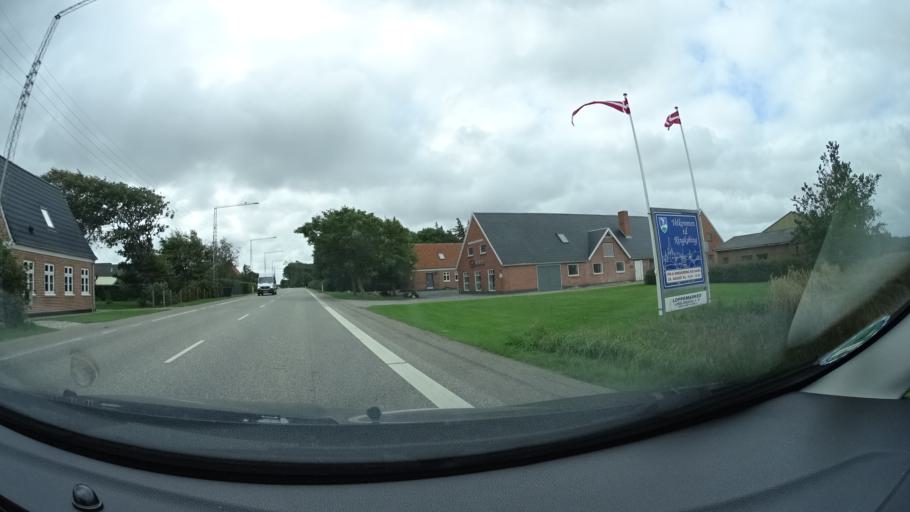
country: DK
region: Central Jutland
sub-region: Ringkobing-Skjern Kommune
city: Ringkobing
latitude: 56.1033
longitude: 8.2573
